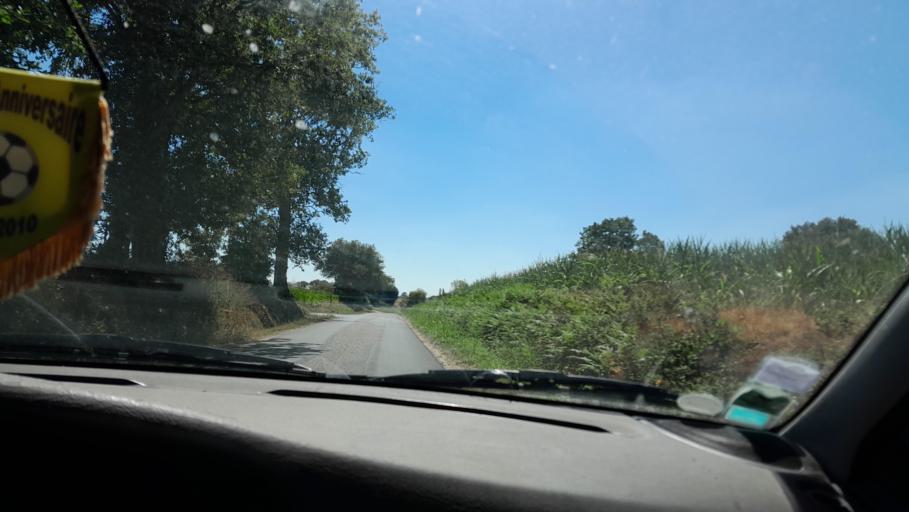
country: FR
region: Pays de la Loire
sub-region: Departement de la Mayenne
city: Congrier
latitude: 47.8211
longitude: -1.1971
